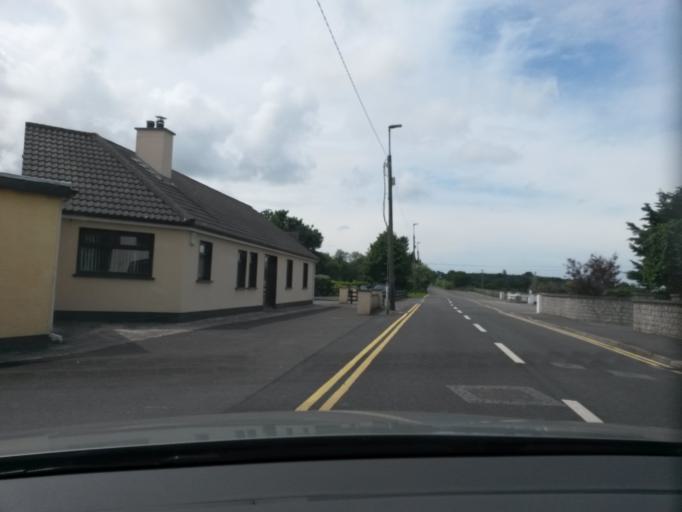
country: IE
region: Connaught
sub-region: County Leitrim
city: Kinlough
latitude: 54.4455
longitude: -8.2878
